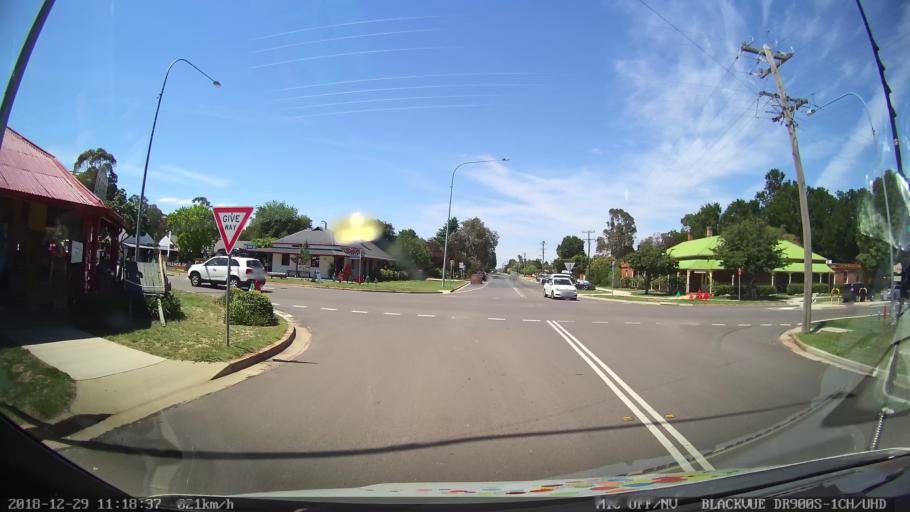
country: AU
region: New South Wales
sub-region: Palerang
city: Bungendore
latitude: -35.2560
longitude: 149.4409
